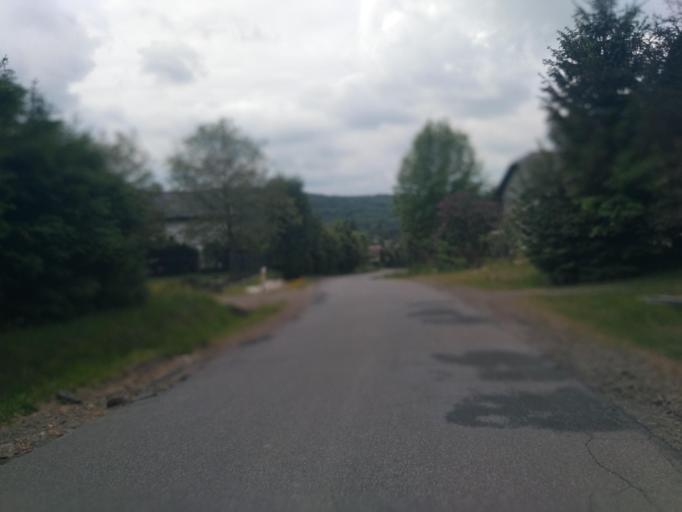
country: PL
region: Subcarpathian Voivodeship
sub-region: Powiat krosnienski
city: Chorkowka
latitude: 49.6662
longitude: 21.6379
